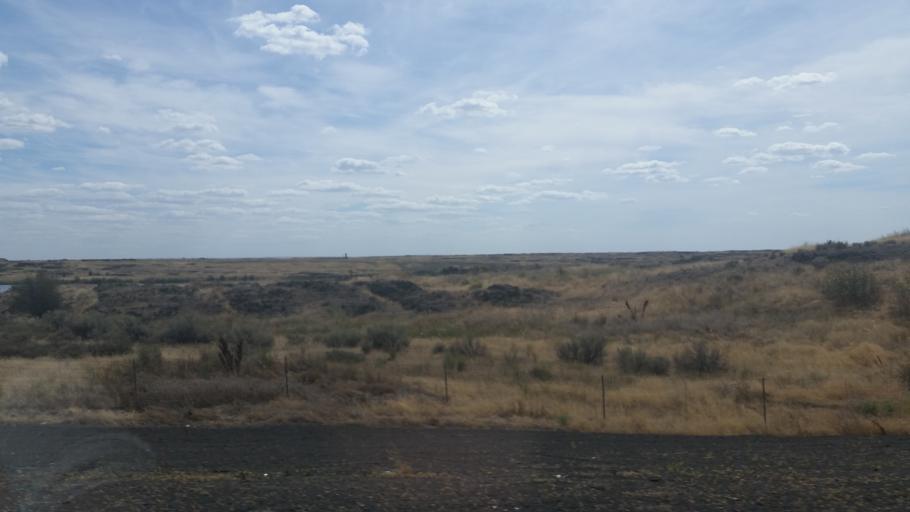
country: US
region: Washington
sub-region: Adams County
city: Ritzville
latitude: 47.2750
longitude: -118.0563
